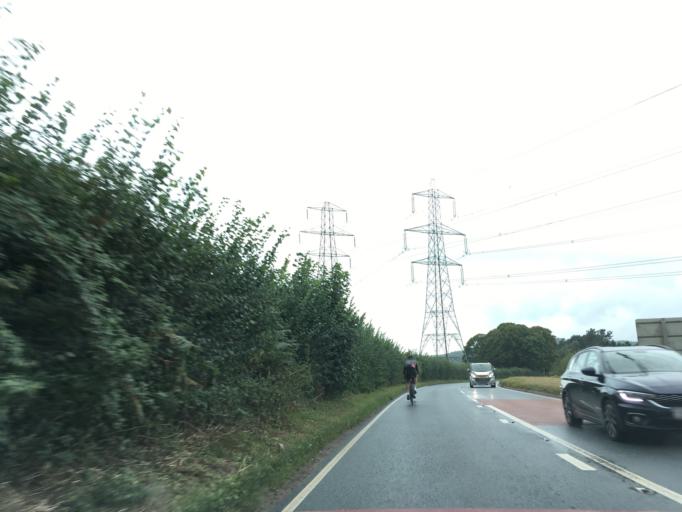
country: GB
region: England
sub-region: Herefordshire
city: Lea
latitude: 51.8959
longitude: -2.5062
